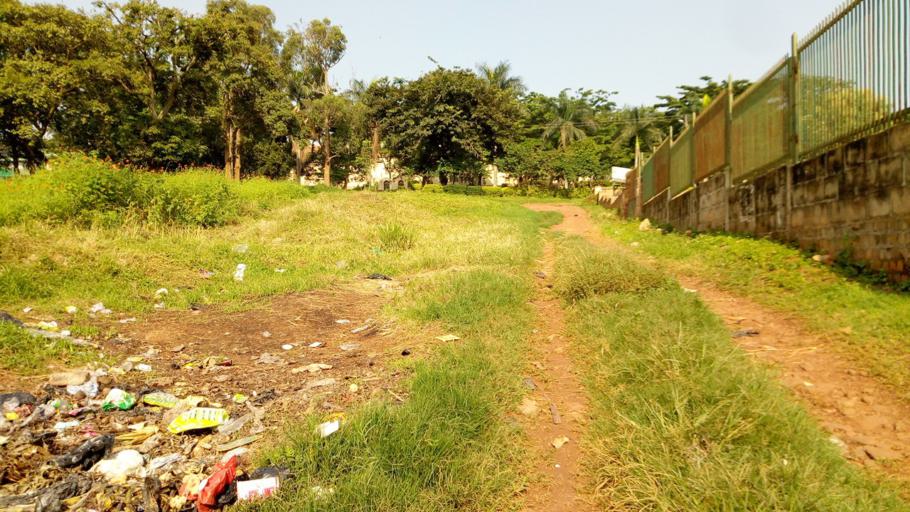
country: UG
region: Central Region
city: Kampala Central Division
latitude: 0.3370
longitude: 32.5712
